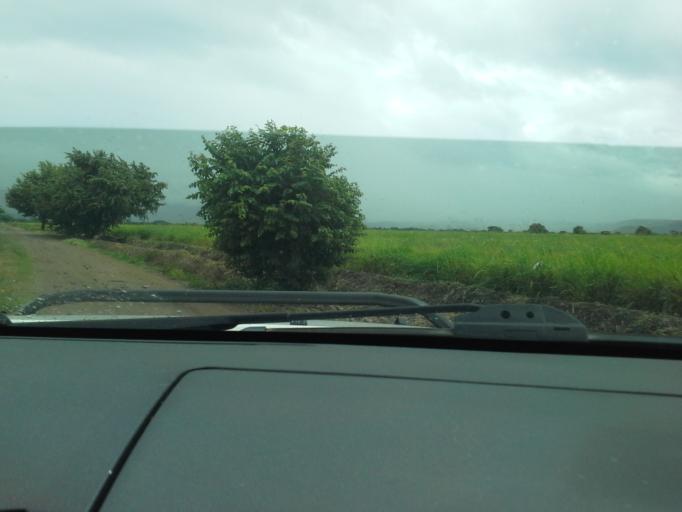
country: NI
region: Matagalpa
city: Ciudad Dario
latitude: 12.8520
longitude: -86.1794
